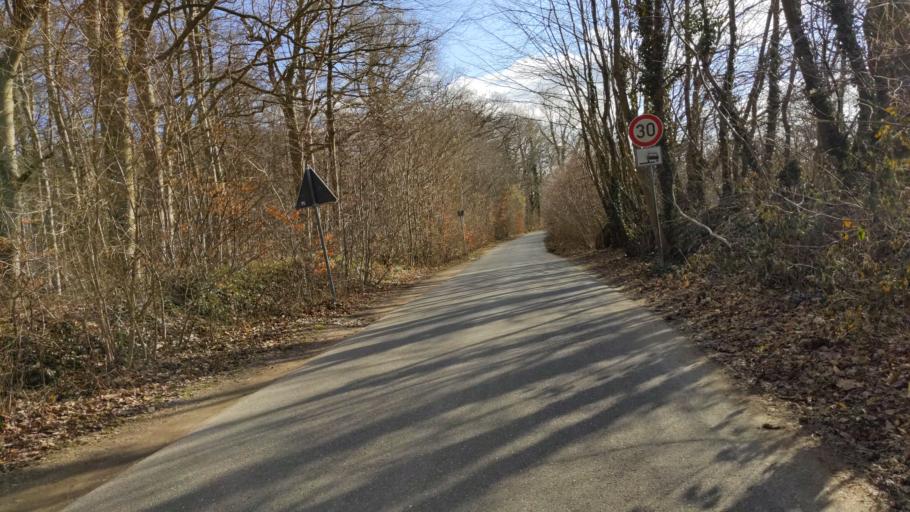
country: DE
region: Schleswig-Holstein
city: Timmendorfer Strand
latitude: 54.0048
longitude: 10.7549
